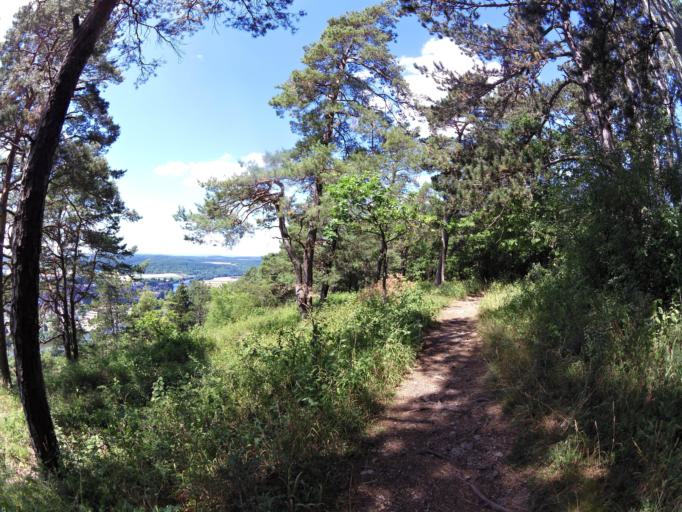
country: DE
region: Bavaria
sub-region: Regierungsbezirk Unterfranken
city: Thungersheim
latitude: 49.8961
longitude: 9.8386
